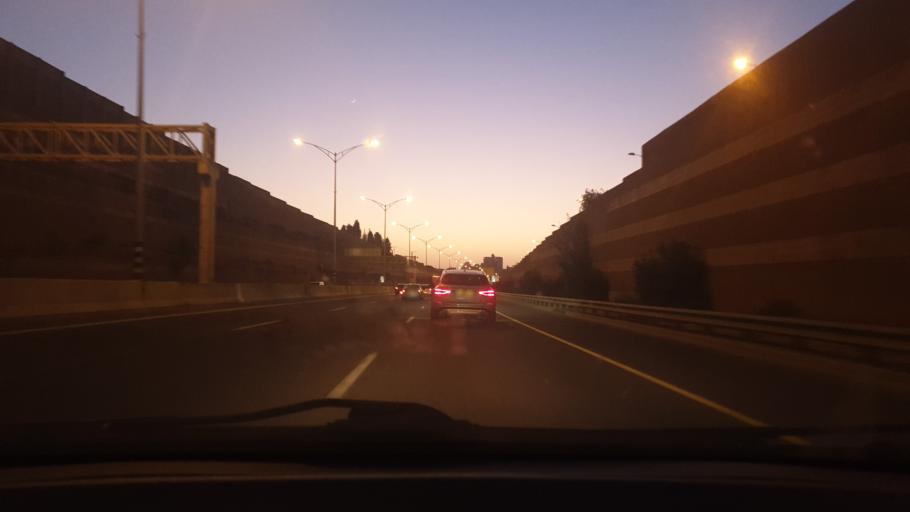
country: IL
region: Tel Aviv
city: Giv`at Shemu'el
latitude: 32.0686
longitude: 34.8579
